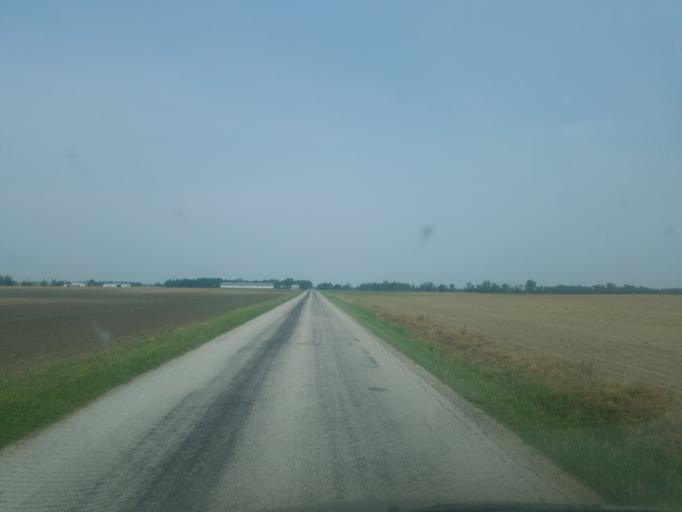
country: US
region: Ohio
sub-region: Marion County
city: Marion
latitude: 40.6894
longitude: -83.1113
